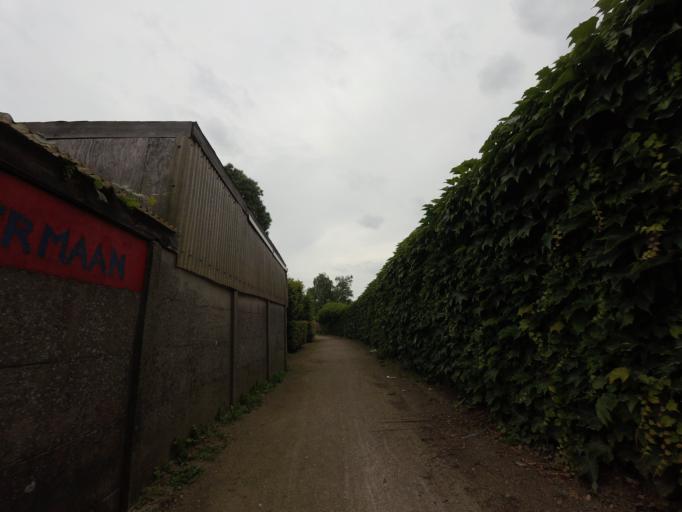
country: BE
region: Flanders
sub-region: Provincie Antwerpen
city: Schilde
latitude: 51.2379
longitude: 4.5852
